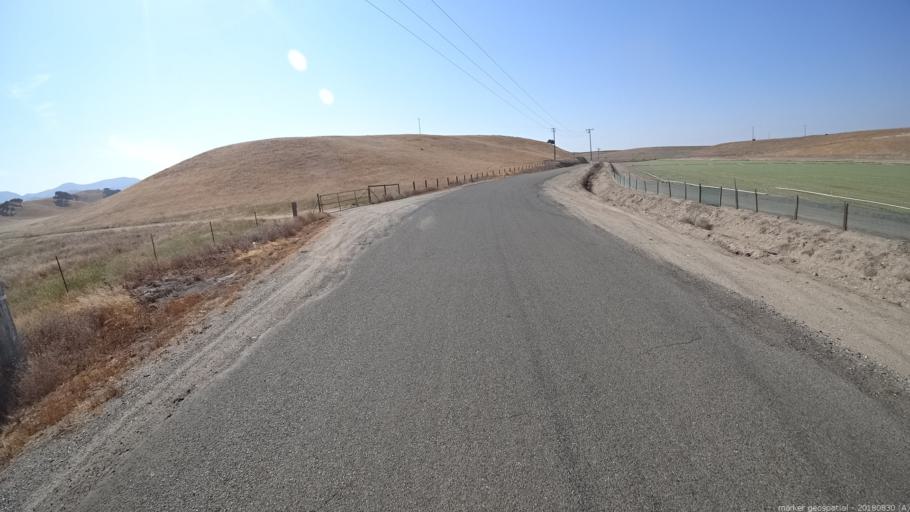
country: US
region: California
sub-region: Monterey County
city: King City
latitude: 36.1071
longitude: -121.0511
